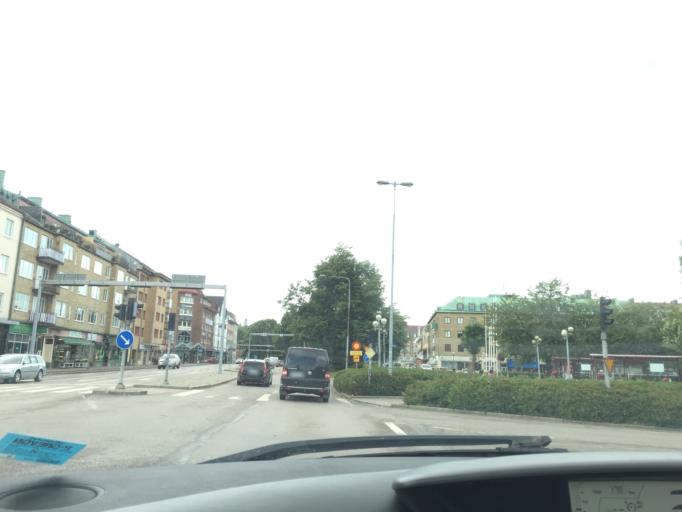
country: SE
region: Vaestra Goetaland
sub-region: Trollhattan
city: Trollhattan
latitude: 58.2827
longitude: 12.2895
